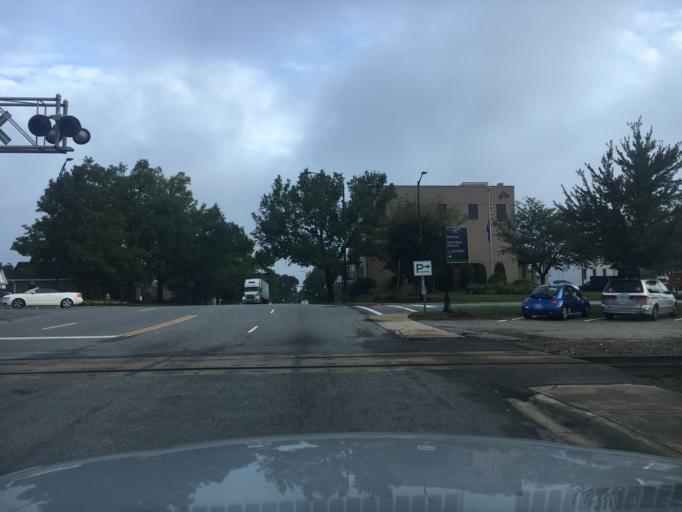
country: US
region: North Carolina
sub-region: Catawba County
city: Hickory
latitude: 35.7317
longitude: -81.3445
